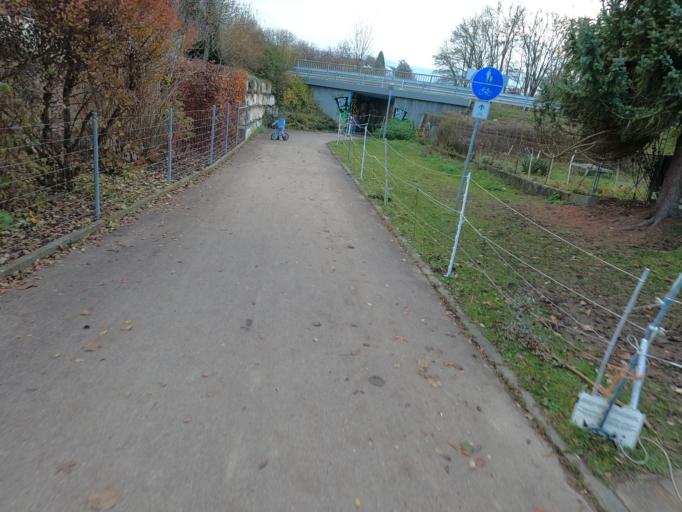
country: DE
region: Baden-Wuerttemberg
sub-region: Regierungsbezirk Stuttgart
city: Boll
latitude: 48.6719
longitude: 9.6093
